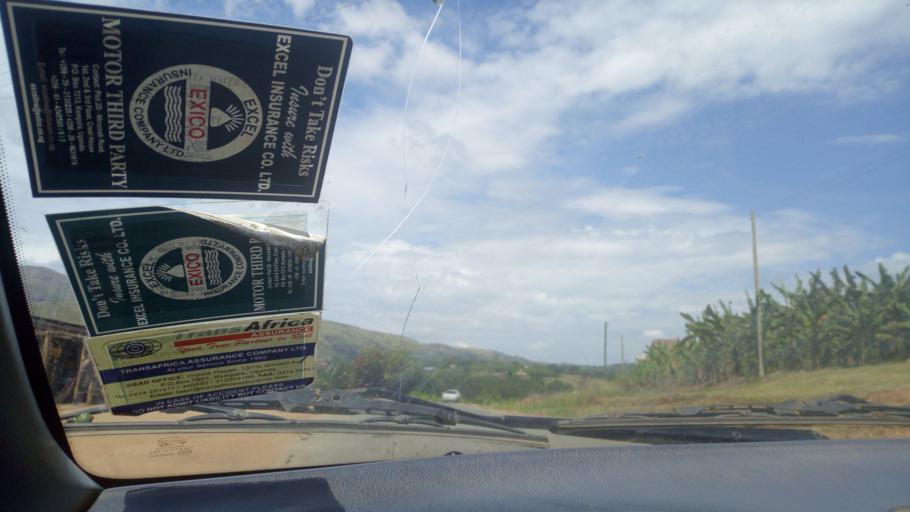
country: UG
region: Western Region
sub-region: Buhweju District
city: Buhweju
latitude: -0.2727
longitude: 30.5632
